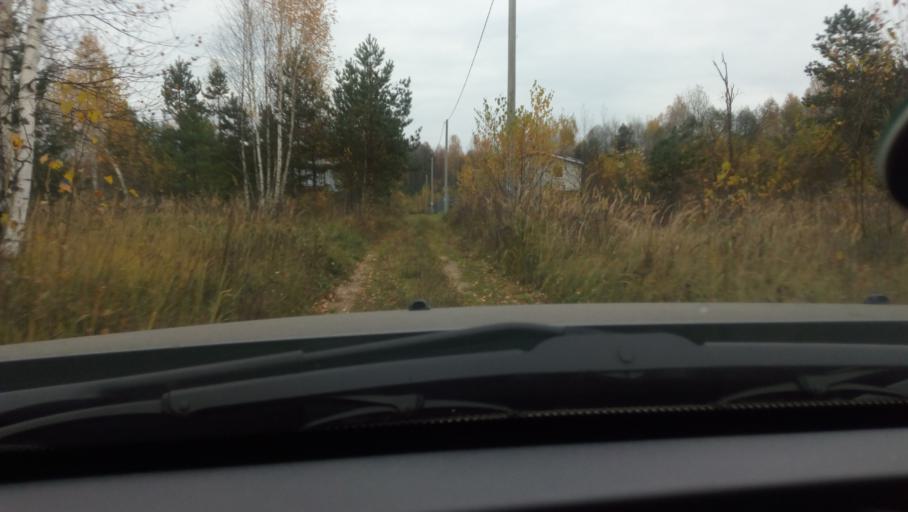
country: RU
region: Moskovskaya
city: Avsyunino
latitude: 55.5793
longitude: 39.2529
